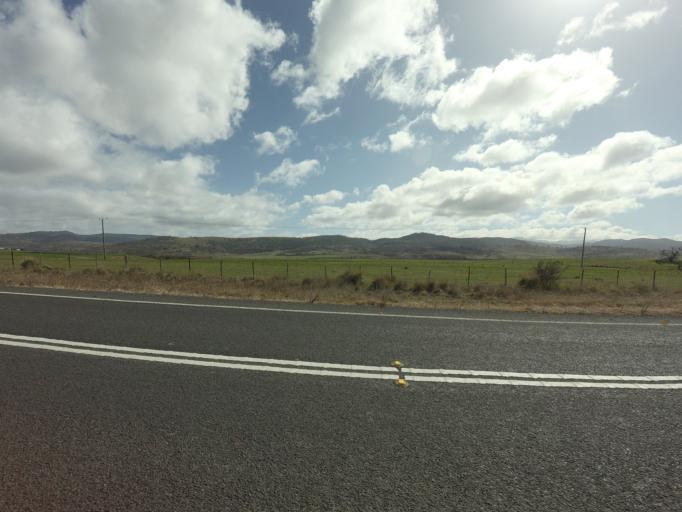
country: AU
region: Tasmania
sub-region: Northern Midlands
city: Evandale
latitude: -41.8064
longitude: 147.6796
